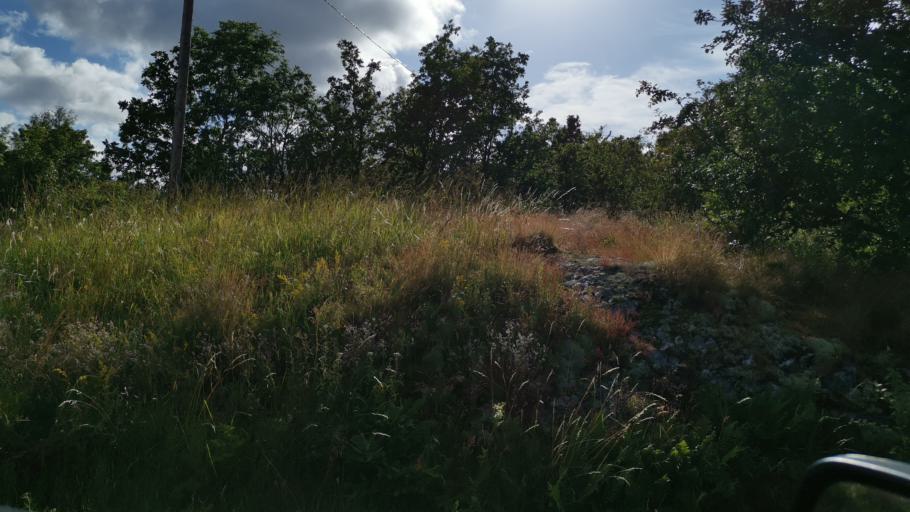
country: SE
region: Vaestra Goetaland
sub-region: Orust
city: Henan
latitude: 58.1482
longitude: 11.6502
